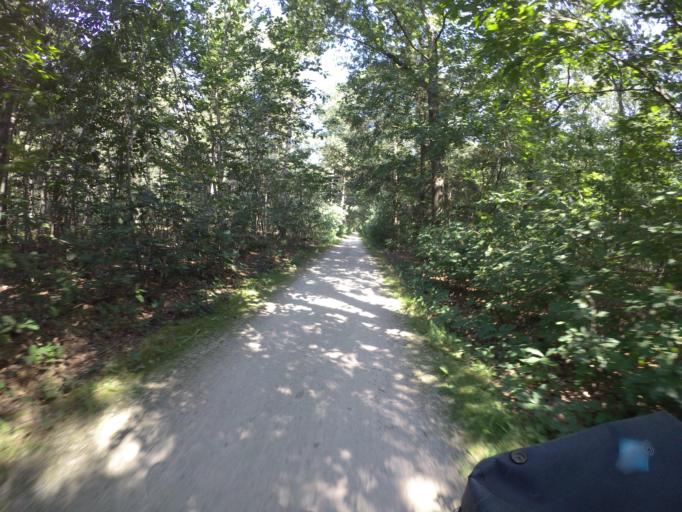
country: NL
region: North Brabant
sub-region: Gemeente Mill en Sint Hubert
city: Wilbertoord
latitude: 51.6169
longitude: 5.7999
